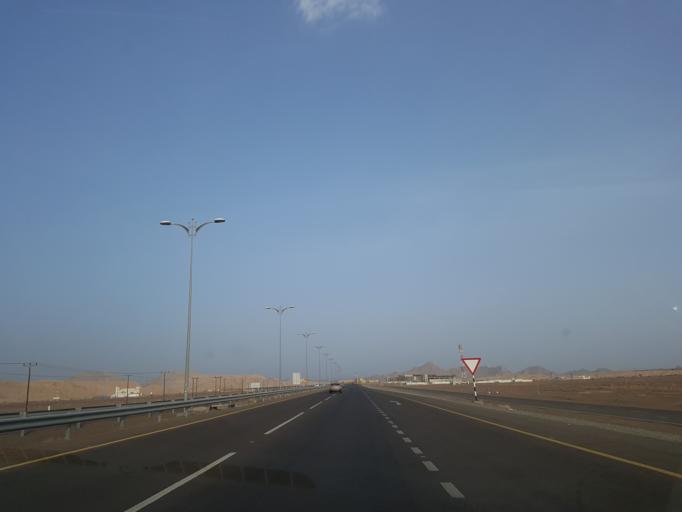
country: OM
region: Al Buraimi
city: Al Buraymi
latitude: 24.2337
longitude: 55.9210
